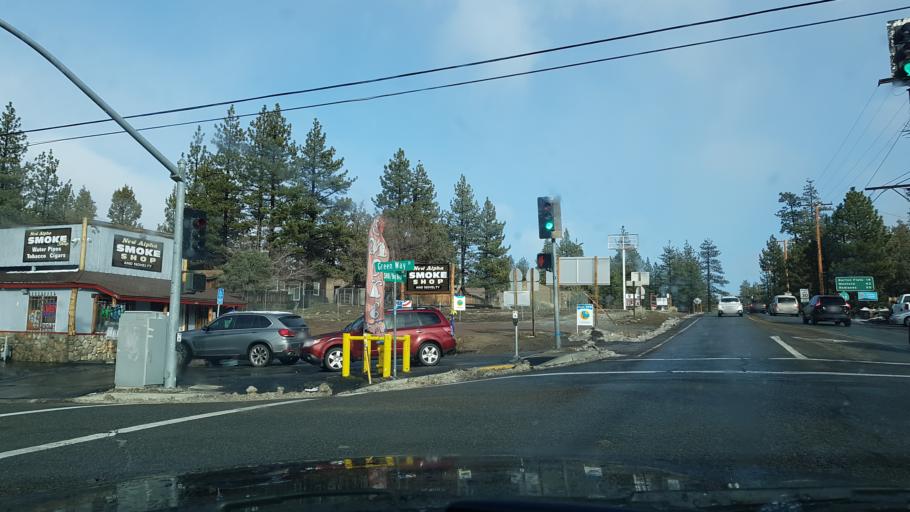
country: US
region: California
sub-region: San Bernardino County
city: Big Bear City
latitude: 34.2611
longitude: -116.8457
